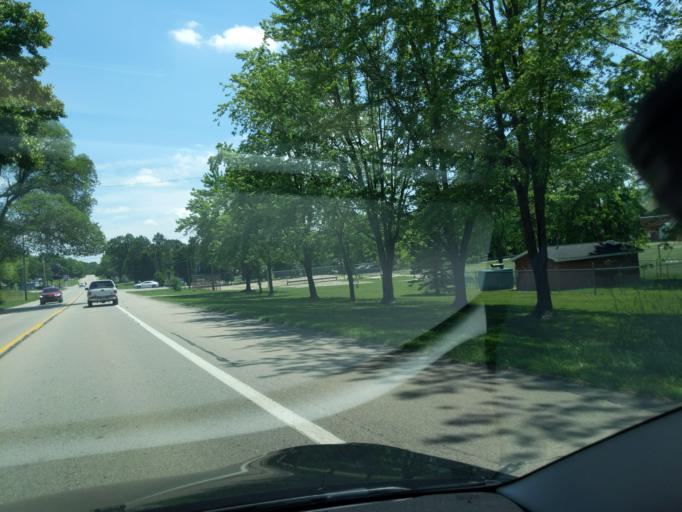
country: US
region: Michigan
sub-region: Ionia County
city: Ionia
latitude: 43.0020
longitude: -84.9401
